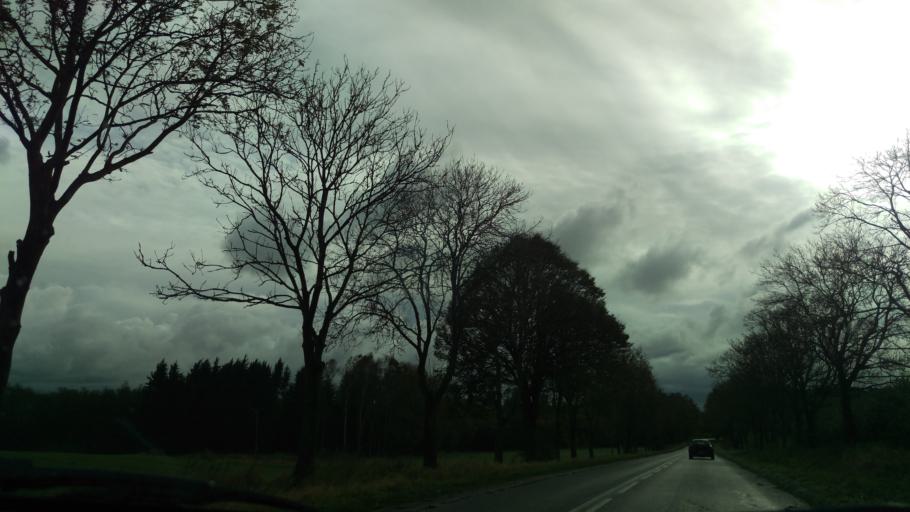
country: PL
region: West Pomeranian Voivodeship
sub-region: Powiat gryficki
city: Gryfice
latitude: 53.8629
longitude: 15.2220
